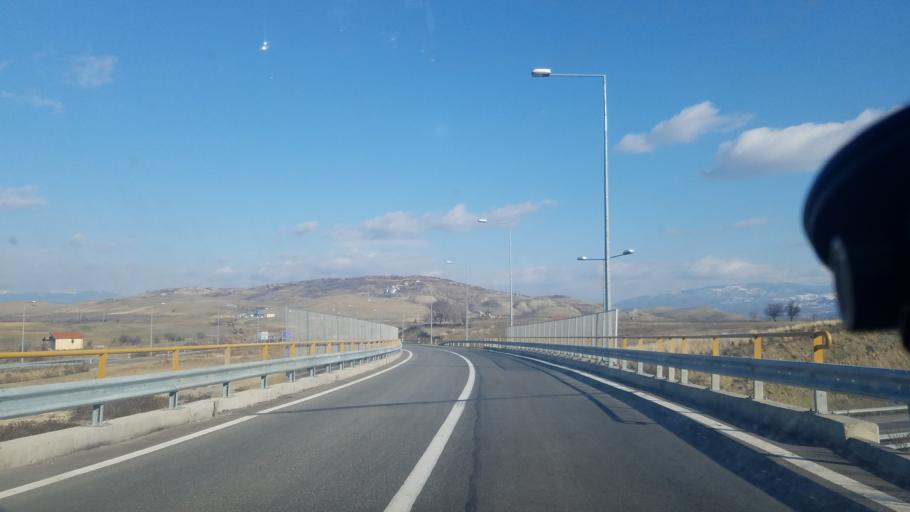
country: MK
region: Stip
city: Shtip
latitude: 41.7807
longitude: 22.1259
